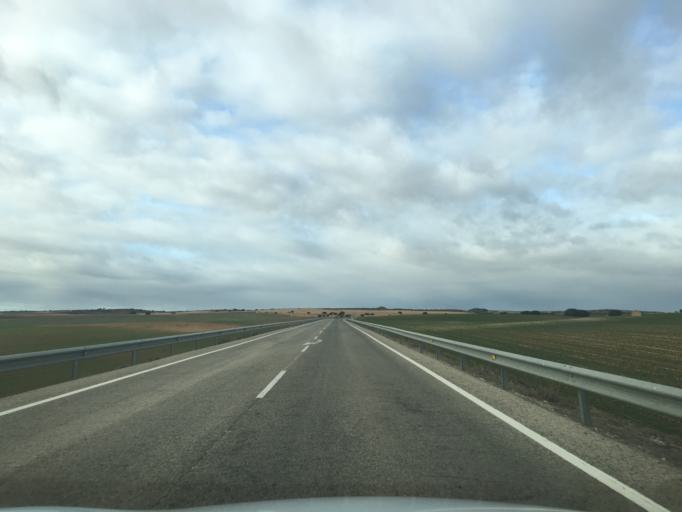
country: ES
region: Castille-La Mancha
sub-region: Provincia de Albacete
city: Petrola
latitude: 38.8255
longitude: -1.5778
